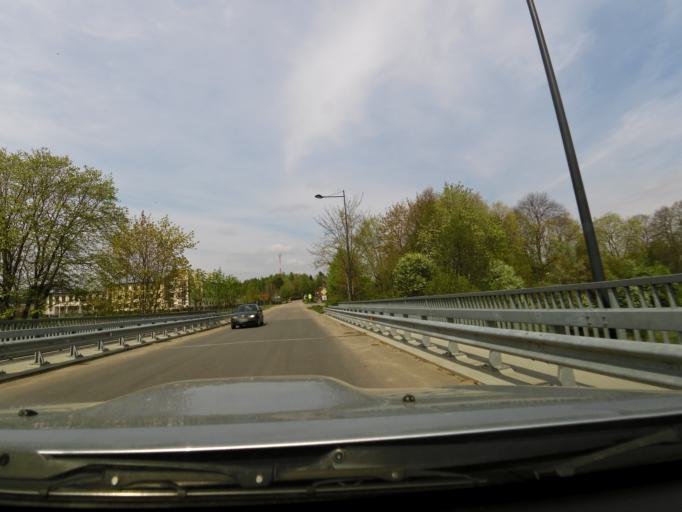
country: LT
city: Salcininkai
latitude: 54.4346
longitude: 25.3001
